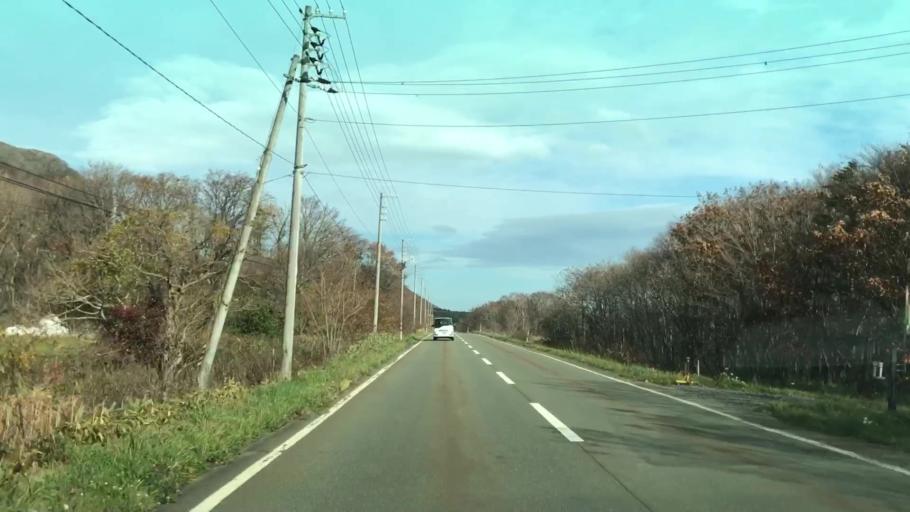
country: JP
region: Hokkaido
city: Obihiro
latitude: 42.0252
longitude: 143.2664
